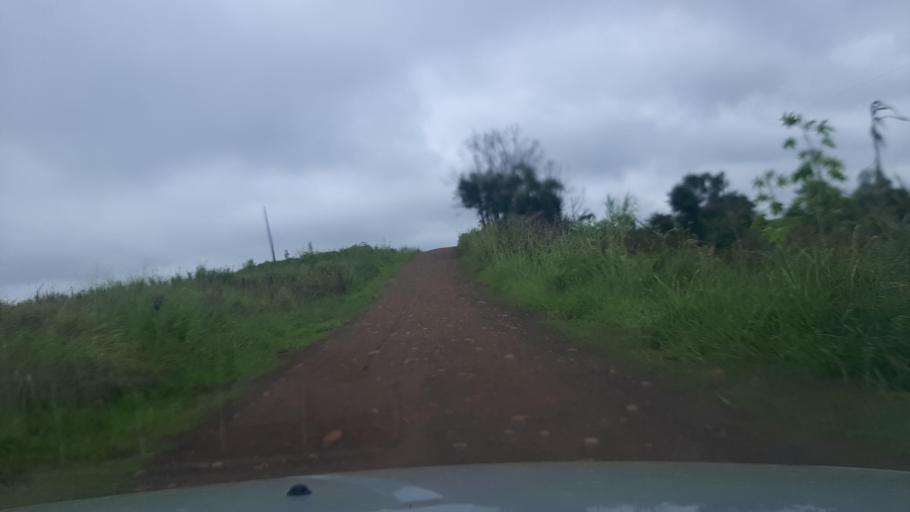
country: BR
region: Parana
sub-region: Ampere
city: Ampere
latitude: -26.0559
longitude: -53.5530
